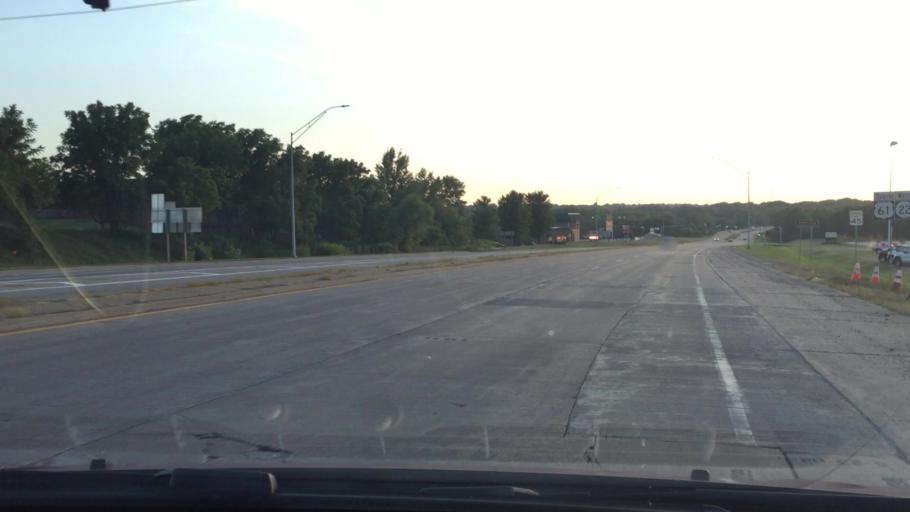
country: US
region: Iowa
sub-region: Muscatine County
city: Muscatine
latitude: 41.4537
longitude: -91.0305
